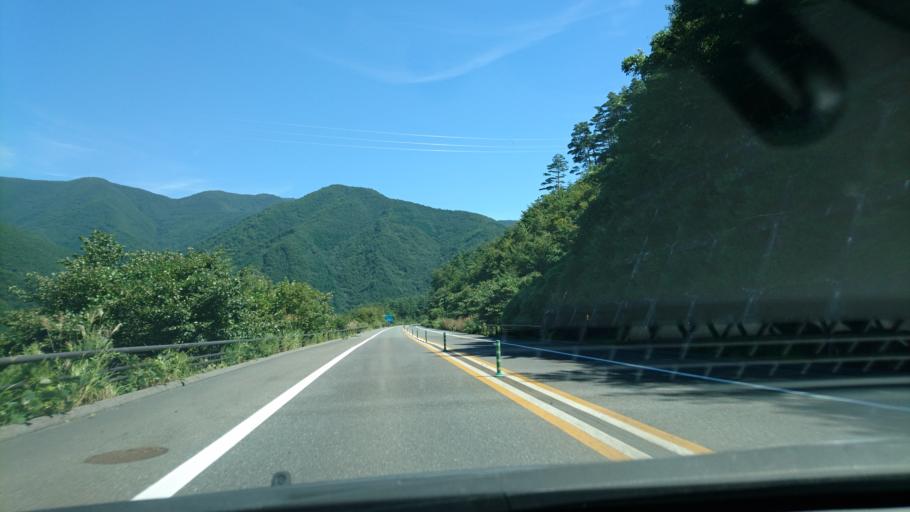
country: JP
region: Iwate
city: Kamaishi
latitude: 39.2479
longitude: 141.7454
